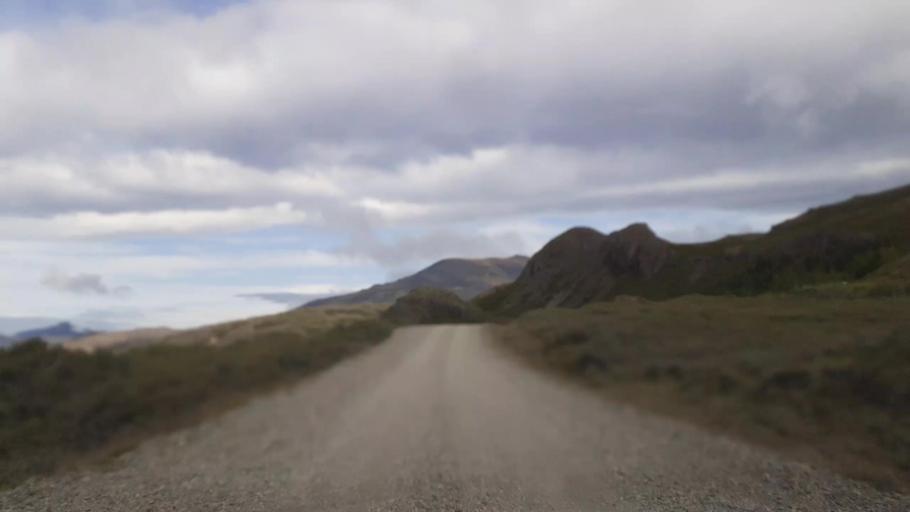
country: IS
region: East
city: Hoefn
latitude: 64.4282
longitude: -14.8853
